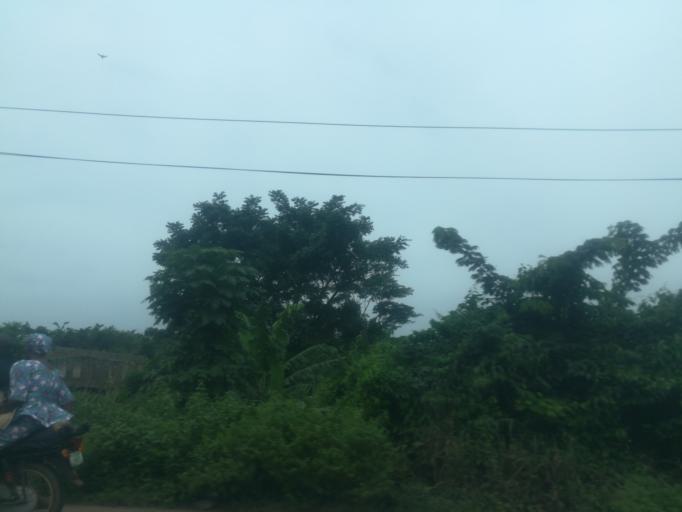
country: NG
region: Oyo
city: Egbeda
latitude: 7.3814
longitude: 3.9998
